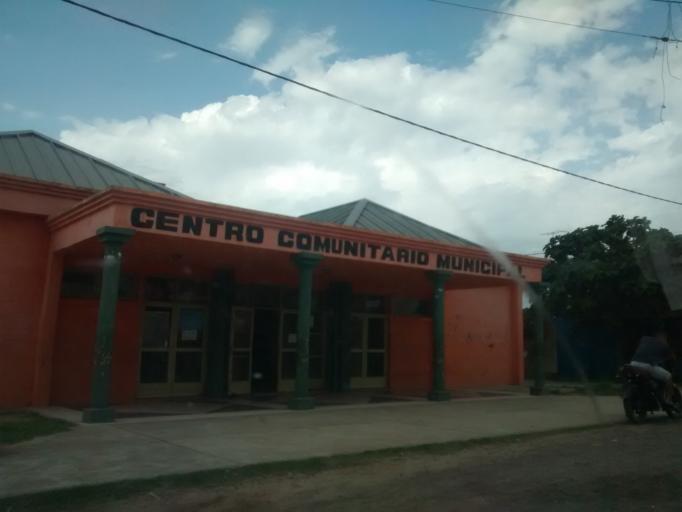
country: AR
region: Chaco
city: Resistencia
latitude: -27.4271
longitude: -58.9771
